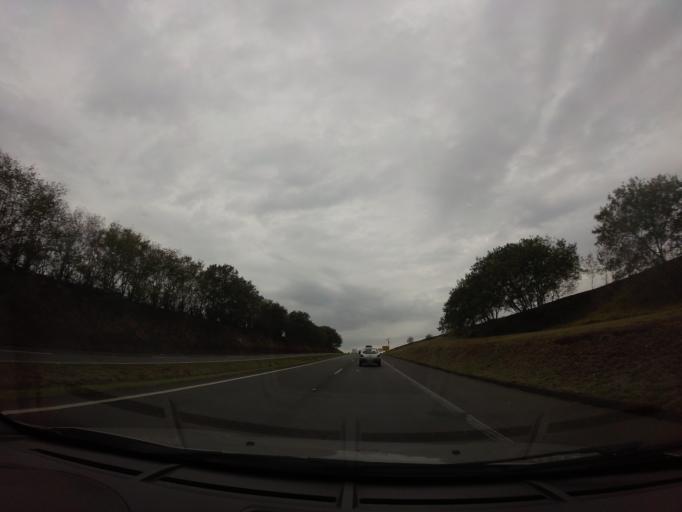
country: BR
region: Sao Paulo
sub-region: Piracicaba
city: Piracicaba
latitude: -22.7250
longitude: -47.5746
